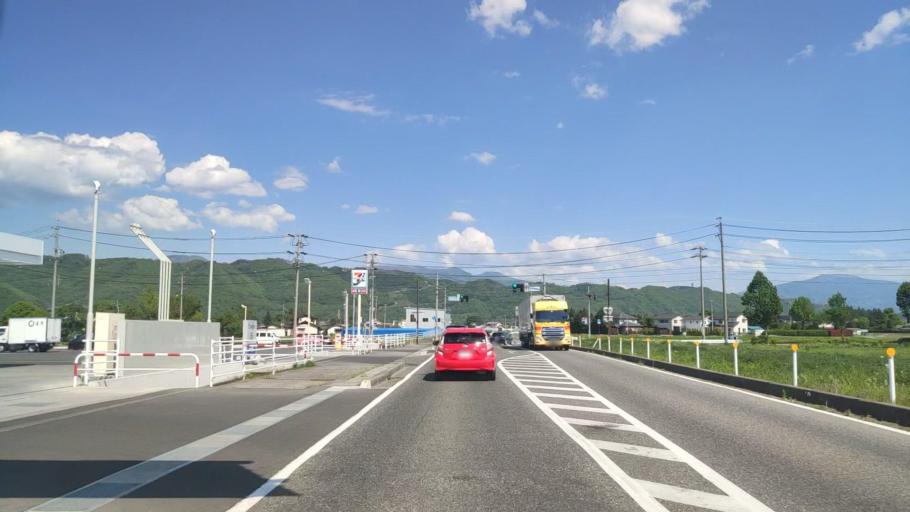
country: JP
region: Nagano
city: Toyoshina
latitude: 36.2800
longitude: 137.9199
